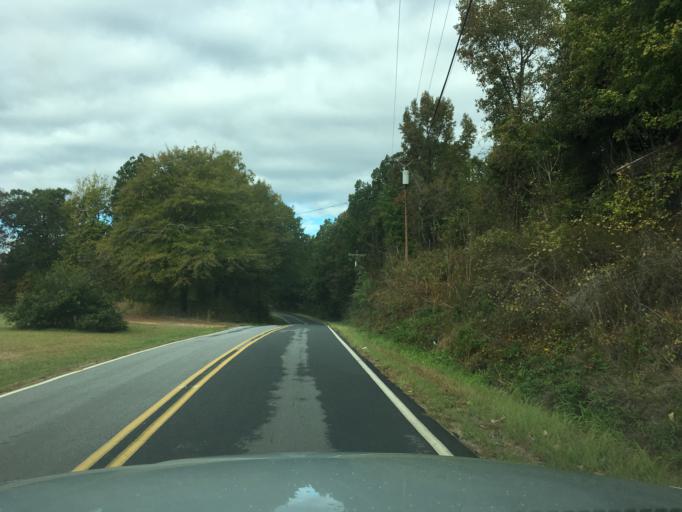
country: US
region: South Carolina
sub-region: Greenville County
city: Tigerville
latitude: 35.0696
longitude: -82.2913
